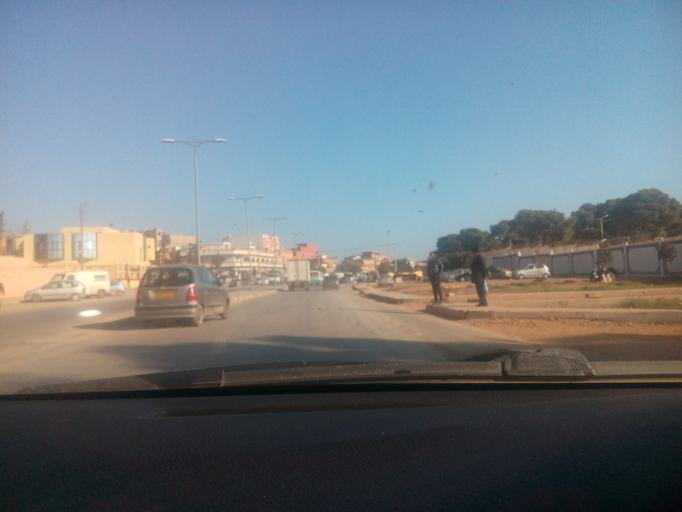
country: DZ
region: Oran
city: Oran
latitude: 35.6588
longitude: -0.6962
